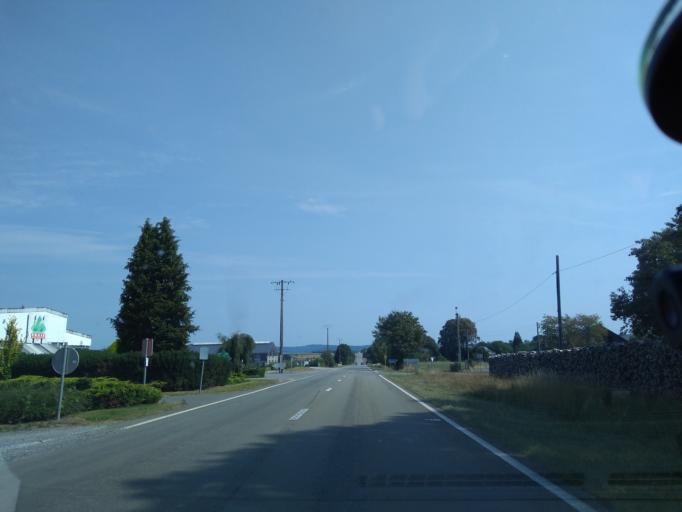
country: BE
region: Wallonia
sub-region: Province du Luxembourg
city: Tenneville
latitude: 50.1485
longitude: 5.5140
